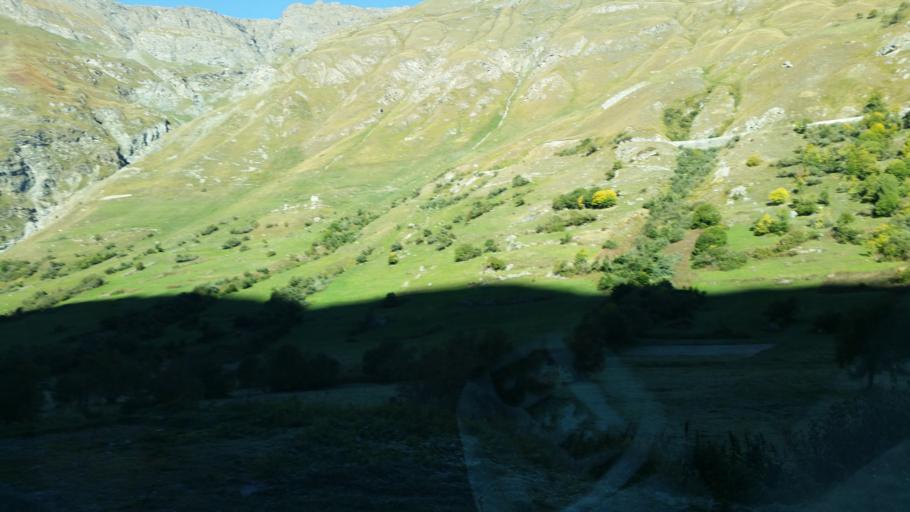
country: FR
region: Rhone-Alpes
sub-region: Departement de la Savoie
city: Val-d'Isere
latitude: 45.3696
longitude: 7.0430
